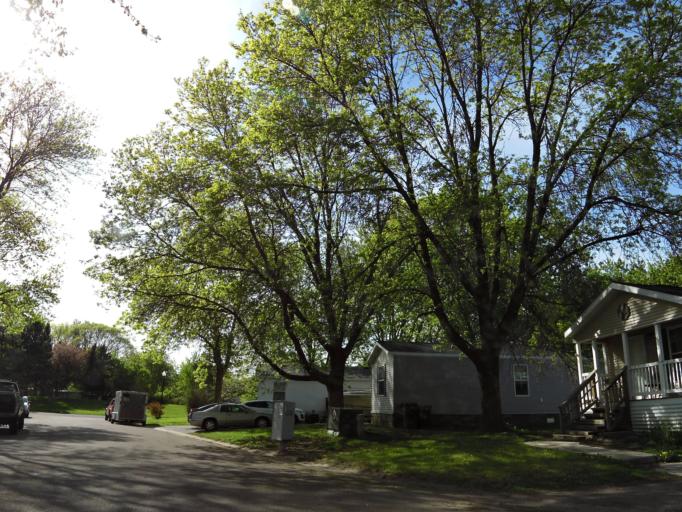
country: US
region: Minnesota
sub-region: Washington County
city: Lake Elmo
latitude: 44.9595
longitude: -92.8719
